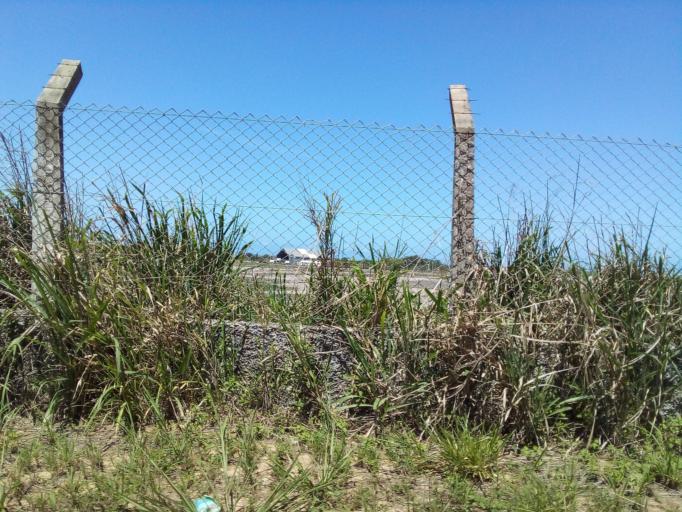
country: BR
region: Espirito Santo
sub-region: Aracruz
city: Aracruz
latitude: -19.8190
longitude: -40.0673
